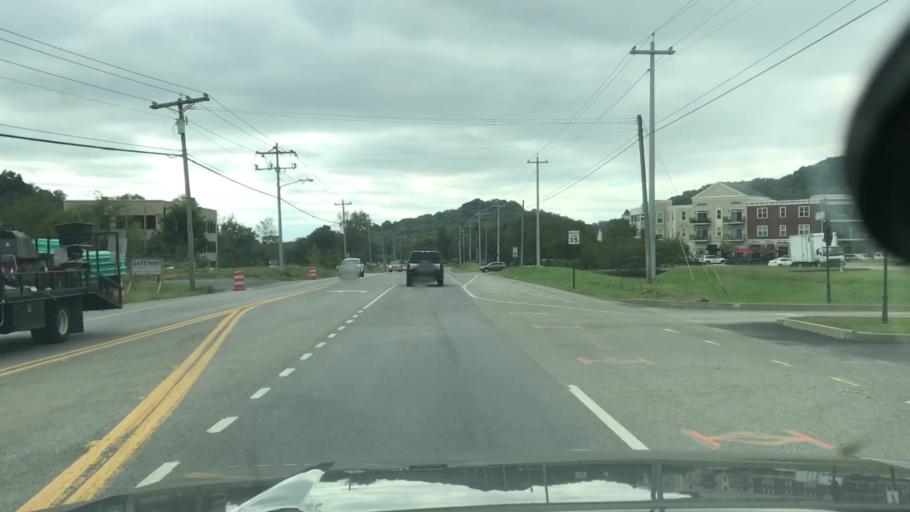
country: US
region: Tennessee
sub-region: Williamson County
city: Franklin
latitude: 35.9723
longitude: -86.8340
